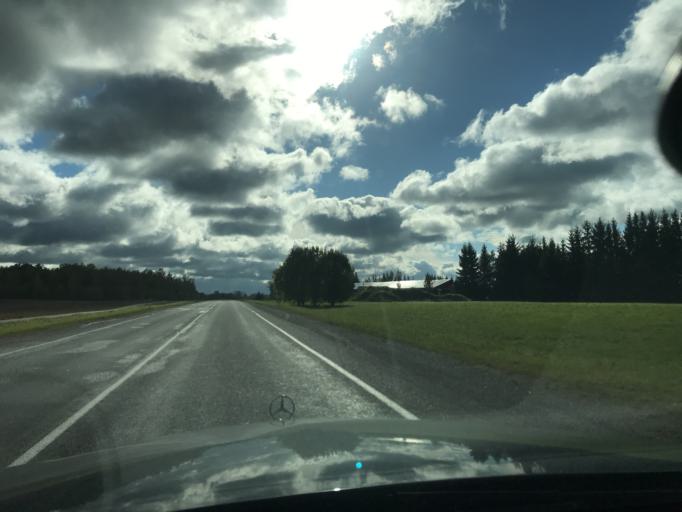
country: EE
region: Vorumaa
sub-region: Antsla vald
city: Vana-Antsla
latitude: 57.9358
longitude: 26.3133
